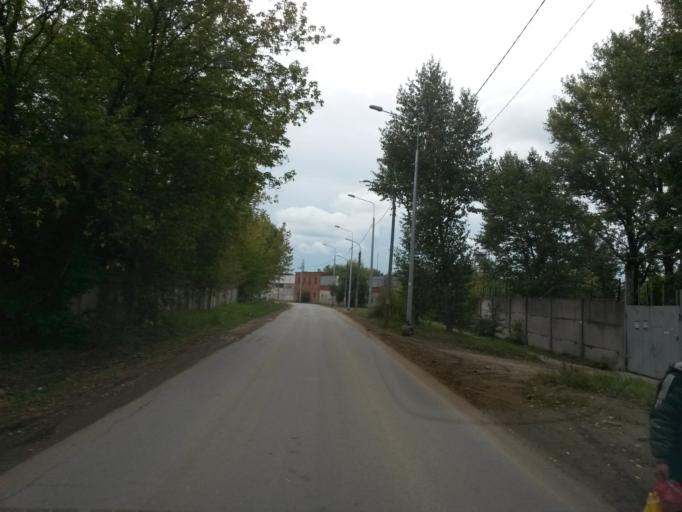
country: RU
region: Moskovskaya
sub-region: Chekhovskiy Rayon
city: Chekhov
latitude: 55.1408
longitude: 37.4797
